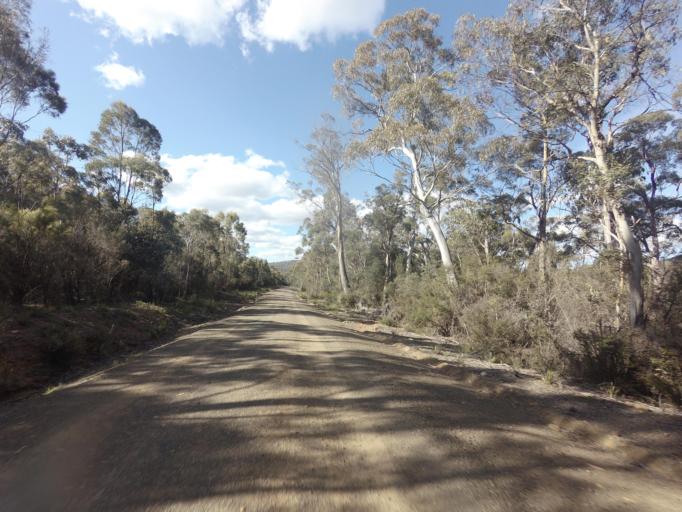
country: AU
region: Tasmania
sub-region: Break O'Day
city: St Helens
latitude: -41.8392
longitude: 148.0158
